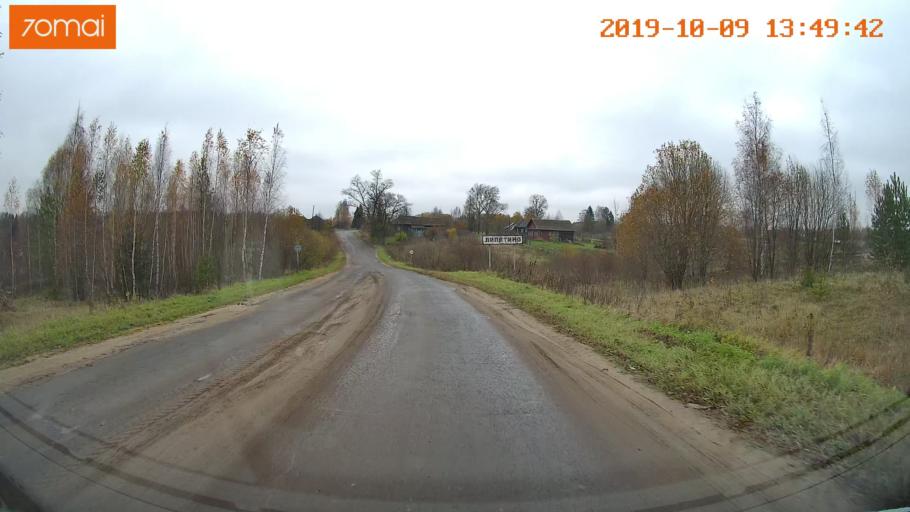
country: RU
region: Kostroma
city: Buy
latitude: 58.4011
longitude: 41.2384
